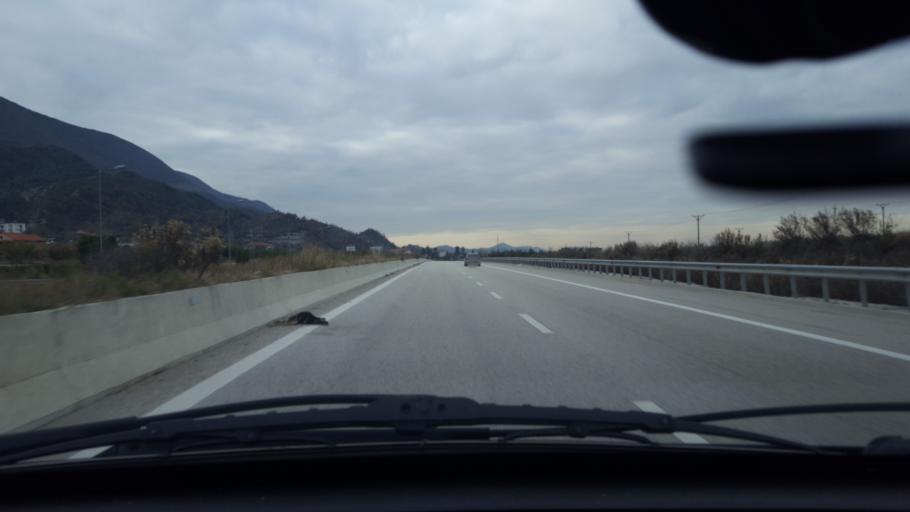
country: AL
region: Tirane
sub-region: Rrethi i Tiranes
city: Berzhite
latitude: 41.2488
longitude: 19.9032
